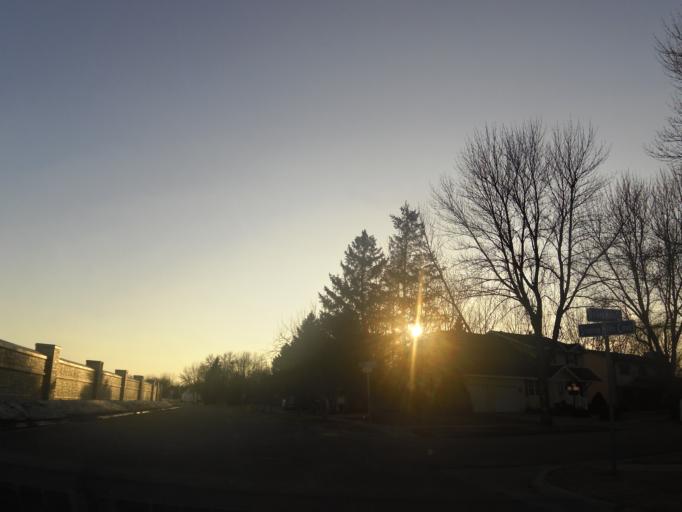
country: US
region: North Dakota
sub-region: Grand Forks County
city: Grand Forks
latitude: 47.8773
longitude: -97.0218
